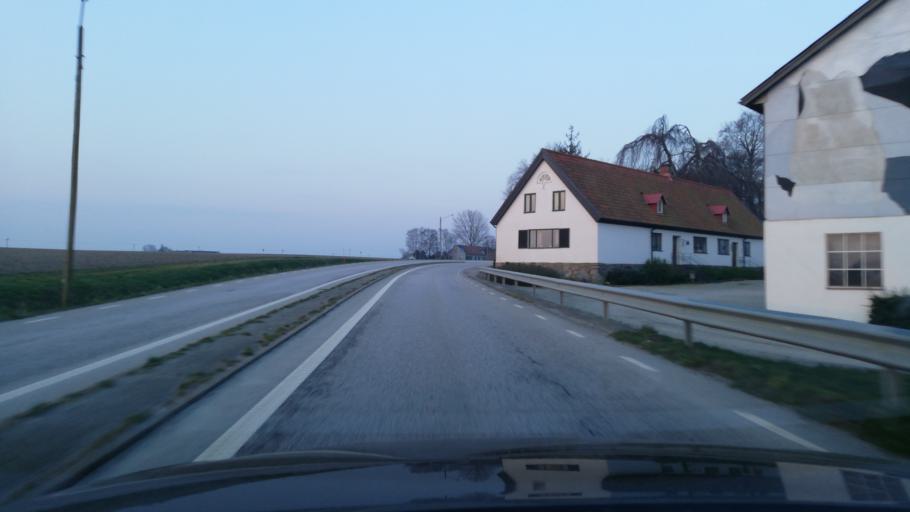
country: SE
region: Skane
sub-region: Tomelilla Kommun
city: Tomelilla
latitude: 55.4926
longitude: 14.1042
